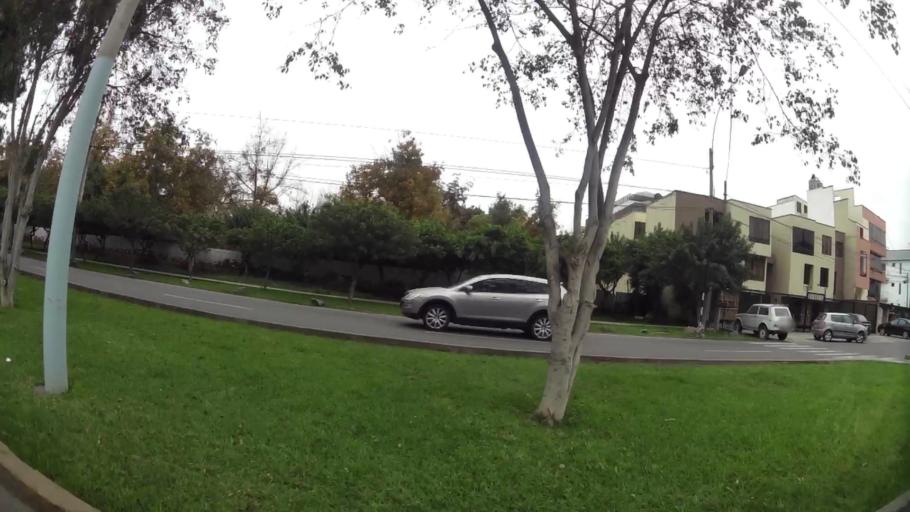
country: PE
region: Lima
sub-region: Lima
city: La Molina
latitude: -12.0740
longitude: -76.9396
